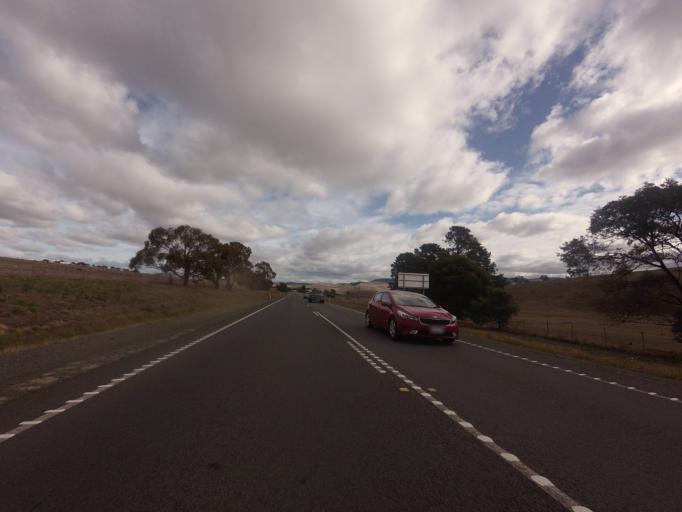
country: AU
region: Tasmania
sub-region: Brighton
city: Bridgewater
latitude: -42.4615
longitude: 147.1907
